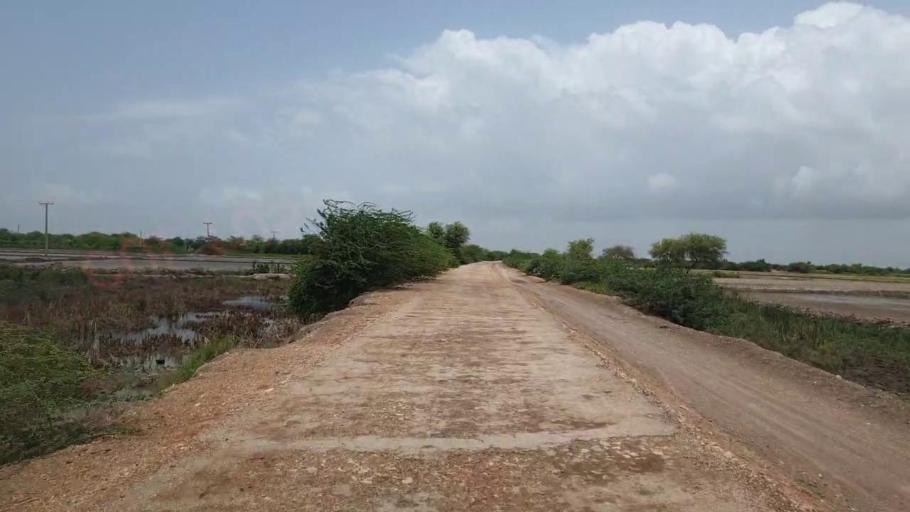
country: PK
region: Sindh
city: Kario
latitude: 24.6930
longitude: 68.6531
